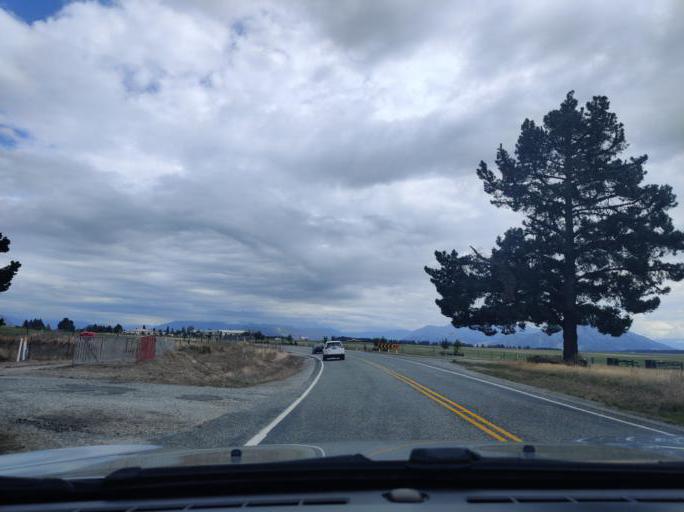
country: NZ
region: Otago
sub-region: Queenstown-Lakes District
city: Wanaka
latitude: -44.7280
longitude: 169.2515
